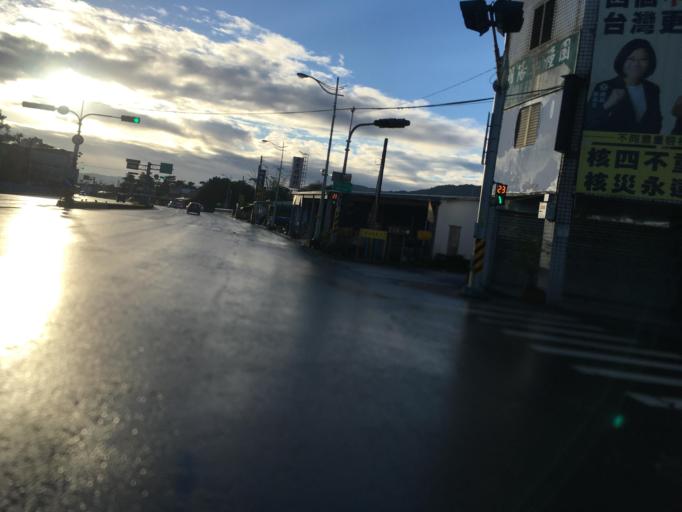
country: TW
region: Taiwan
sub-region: Yilan
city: Yilan
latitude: 24.6350
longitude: 121.7877
